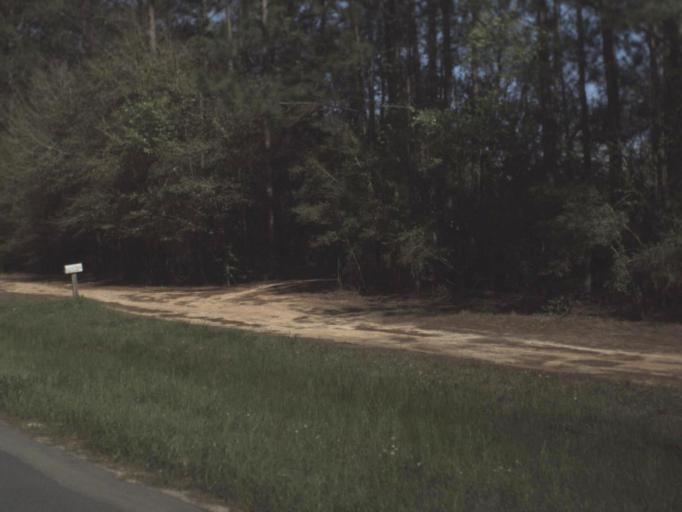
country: US
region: Florida
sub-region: Holmes County
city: Bonifay
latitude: 30.7582
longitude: -85.8780
